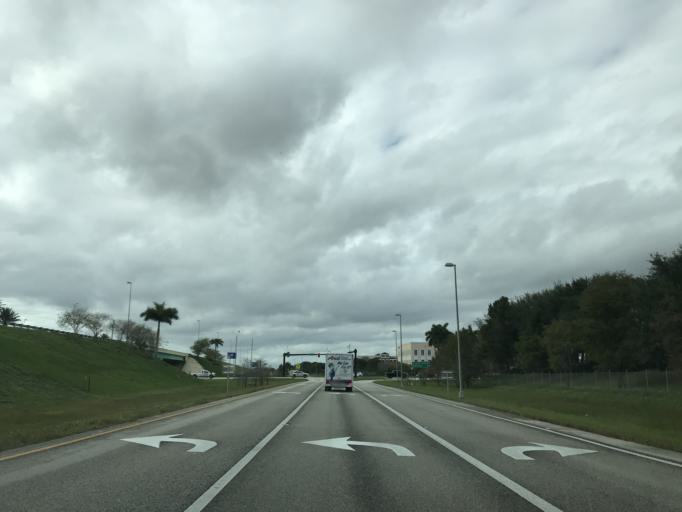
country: US
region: Florida
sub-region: Broward County
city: Coral Springs
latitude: 26.3028
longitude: -80.2772
